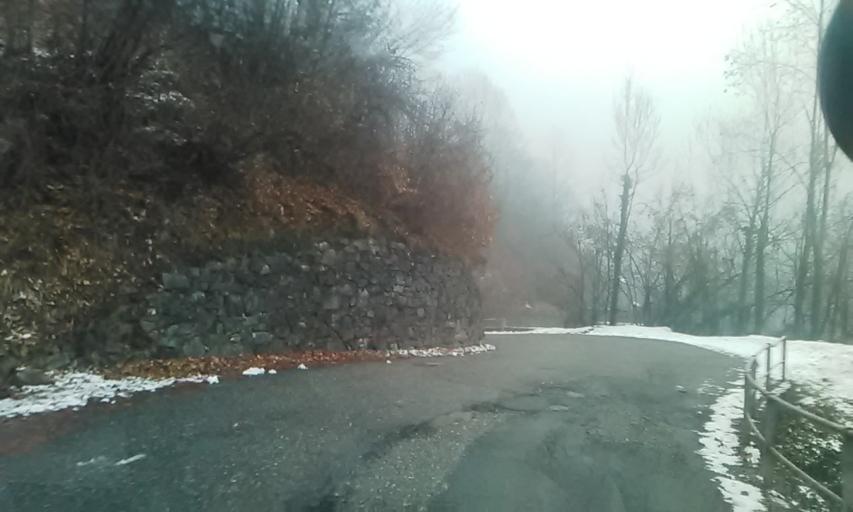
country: IT
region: Piedmont
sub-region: Provincia di Vercelli
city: Varallo
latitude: 45.8389
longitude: 8.2630
